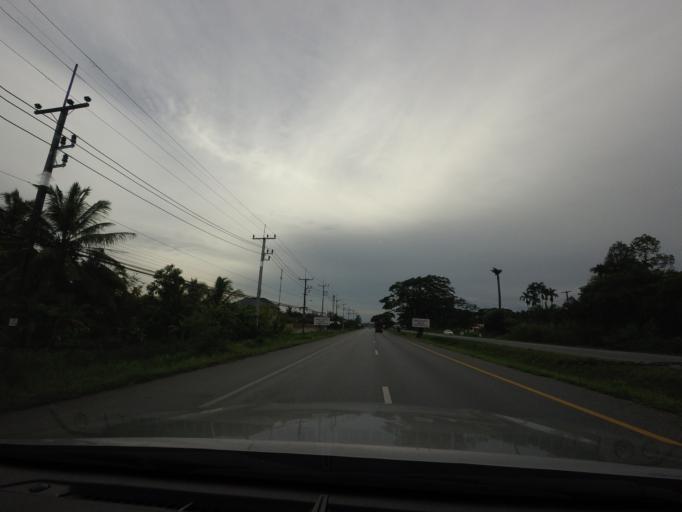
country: TH
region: Nakhon Si Thammarat
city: Chian Yai
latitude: 8.0882
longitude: 100.1371
